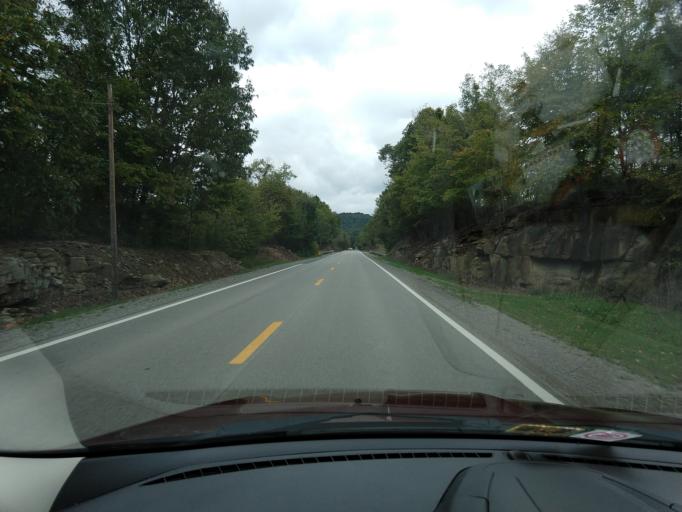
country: US
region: West Virginia
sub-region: Barbour County
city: Philippi
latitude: 39.1200
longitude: -79.9964
